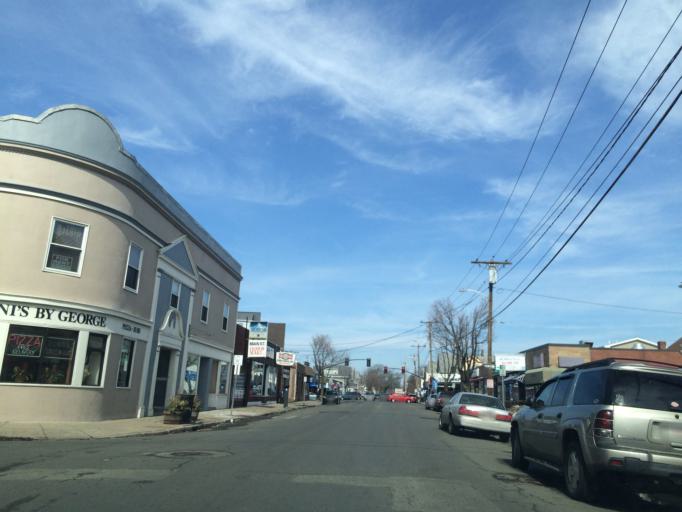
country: US
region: Massachusetts
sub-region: Middlesex County
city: Medford
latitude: 42.4042
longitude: -71.1075
